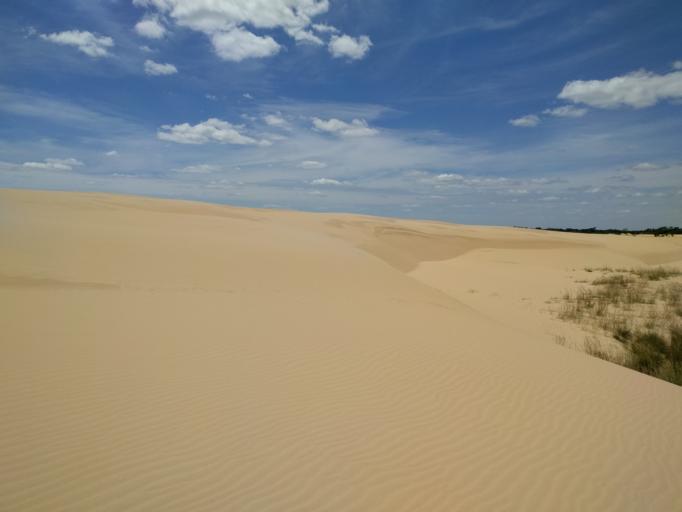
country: BO
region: Santa Cruz
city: Santa Cruz de la Sierra
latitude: -17.9532
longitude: -63.1521
